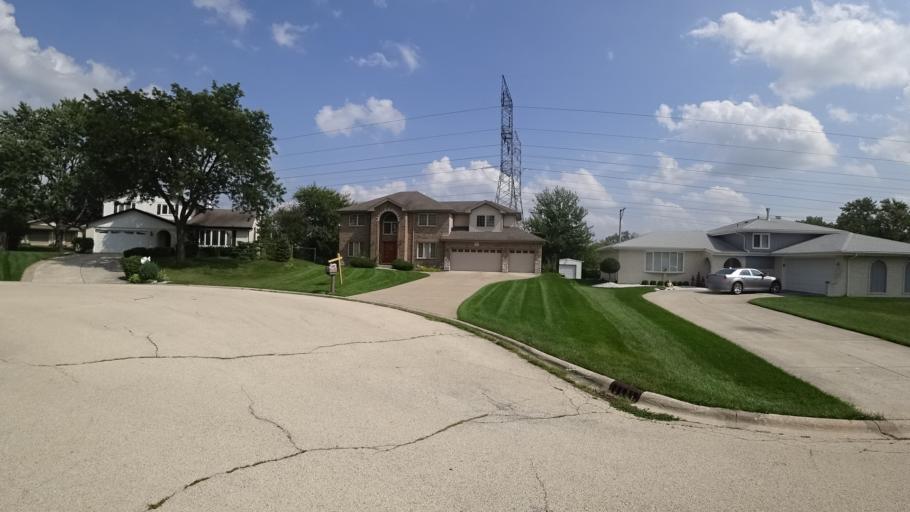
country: US
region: Illinois
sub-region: Will County
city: Goodings Grove
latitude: 41.6394
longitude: -87.9132
